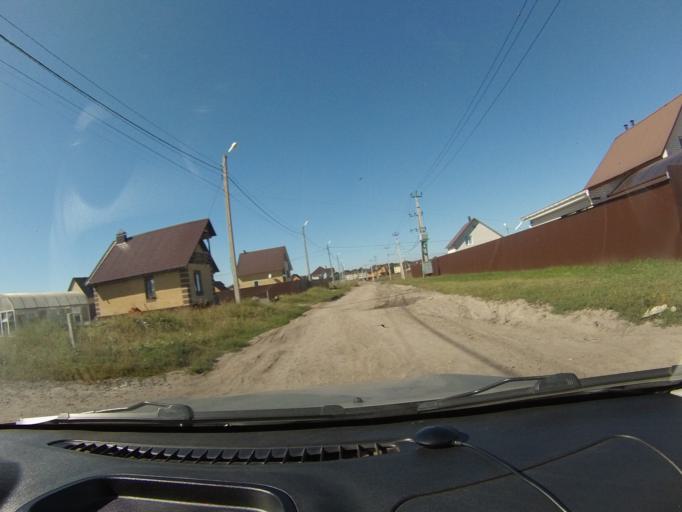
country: RU
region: Tambov
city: Komsomolets
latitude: 52.7798
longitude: 41.3699
